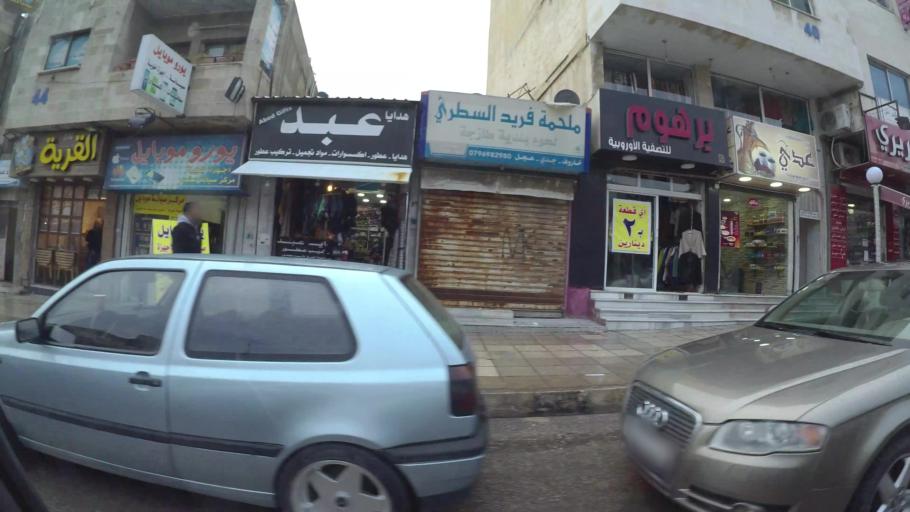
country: JO
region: Amman
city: Al Jubayhah
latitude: 32.0244
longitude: 35.8406
